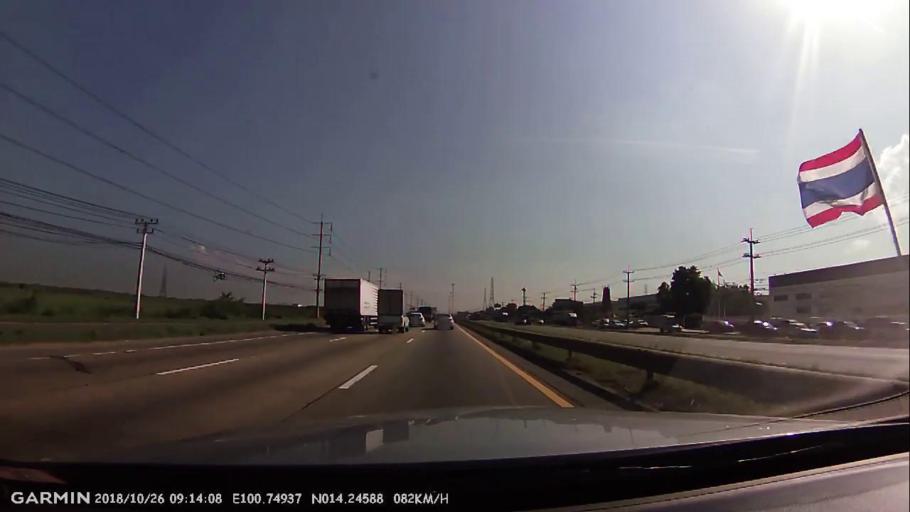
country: TH
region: Phra Nakhon Si Ayutthaya
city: Wang Noi
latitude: 14.2461
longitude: 100.7496
